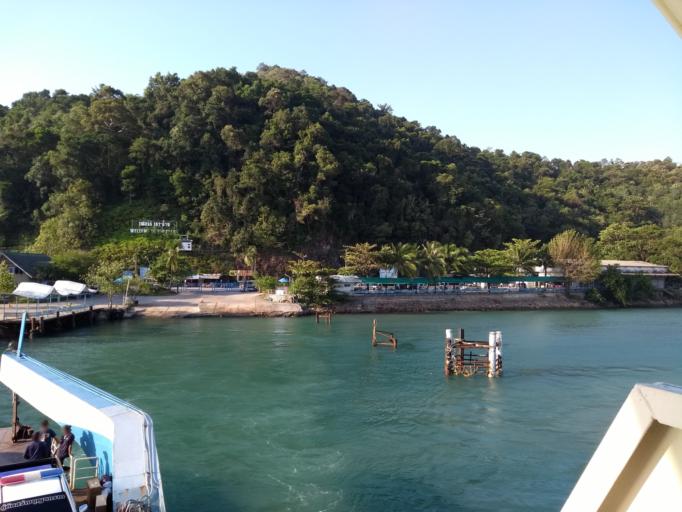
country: TH
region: Trat
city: Laem Ngop
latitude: 12.1424
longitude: 102.2805
